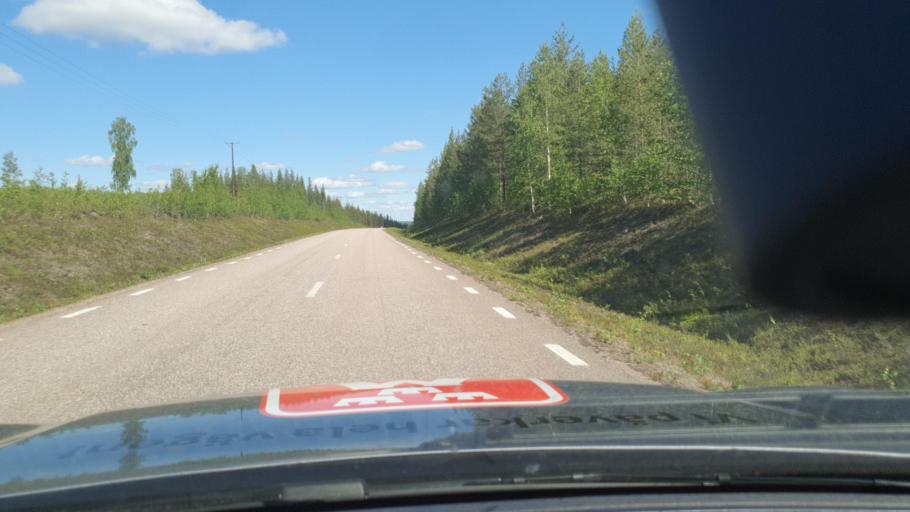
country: SE
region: Norrbotten
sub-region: Overkalix Kommun
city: OEverkalix
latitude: 67.0440
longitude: 22.5020
